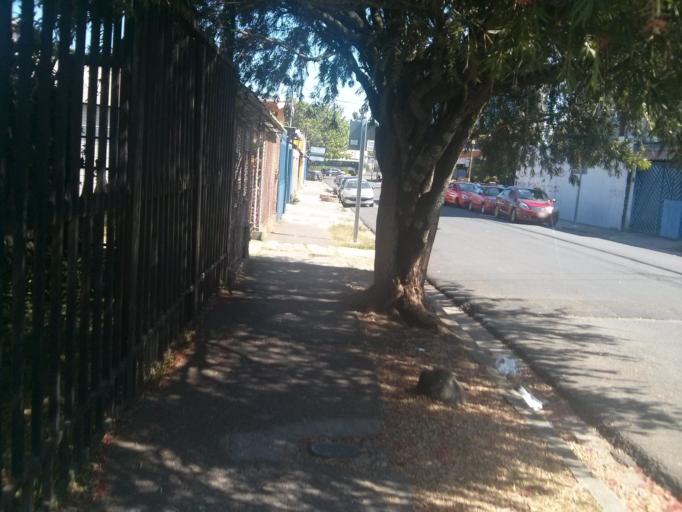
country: CR
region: San Jose
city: San Pedro
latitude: 9.9298
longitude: -84.0465
